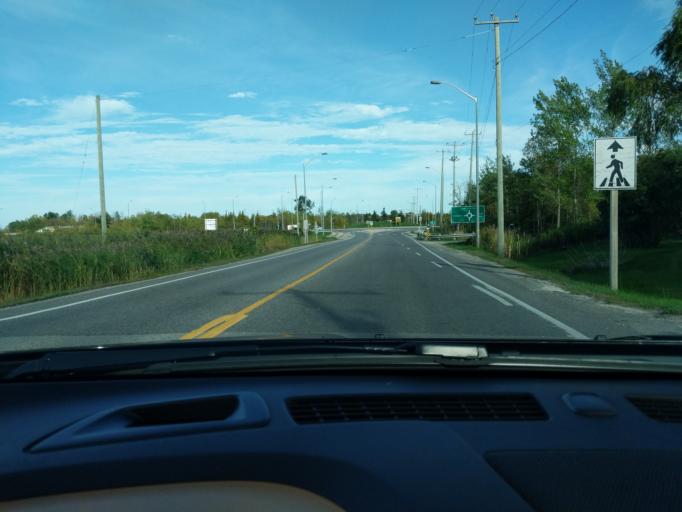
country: CA
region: Ontario
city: Collingwood
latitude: 44.4867
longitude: -80.1760
